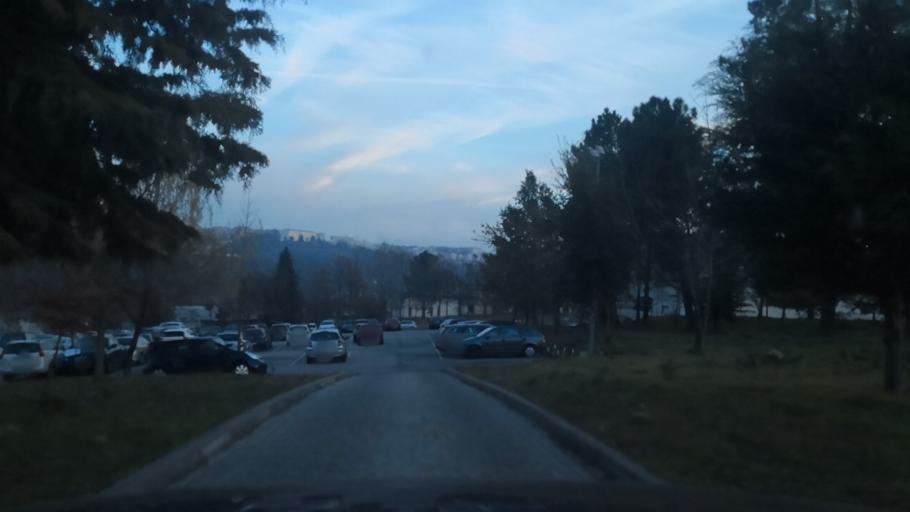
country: PT
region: Vila Real
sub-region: Vila Real
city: Vila Real
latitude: 41.3116
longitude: -7.7622
